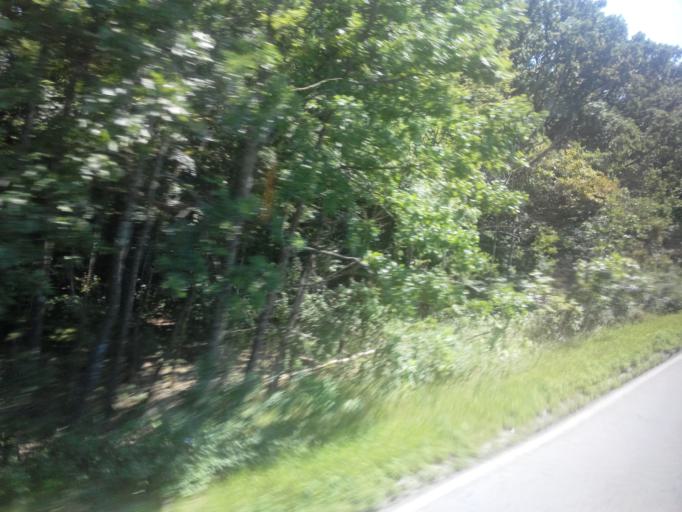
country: RO
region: Timis
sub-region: Comuna Barna
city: Barna
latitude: 45.7575
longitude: 22.0124
